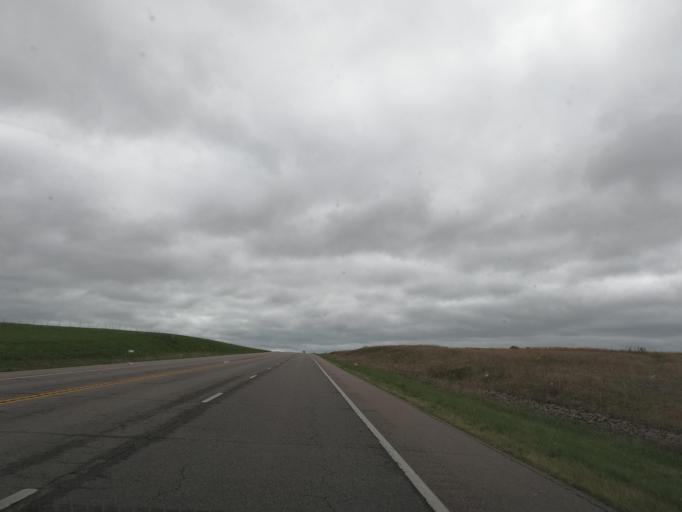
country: US
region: Kansas
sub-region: Greenwood County
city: Eureka
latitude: 37.6496
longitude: -96.4553
